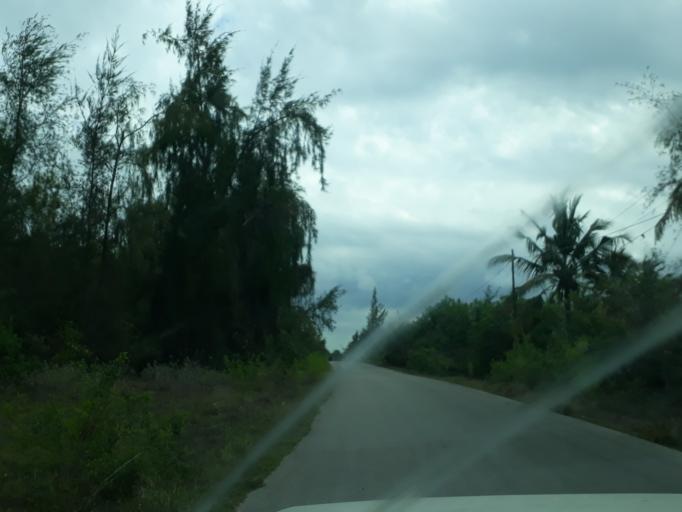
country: TZ
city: Kiwengwa
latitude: -6.0802
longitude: 39.4262
